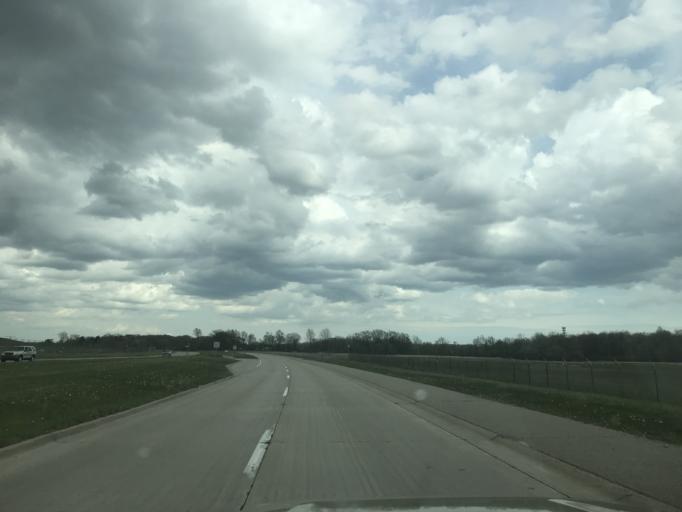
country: US
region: Michigan
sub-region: Wayne County
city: Romulus
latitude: 42.1910
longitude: -83.3575
